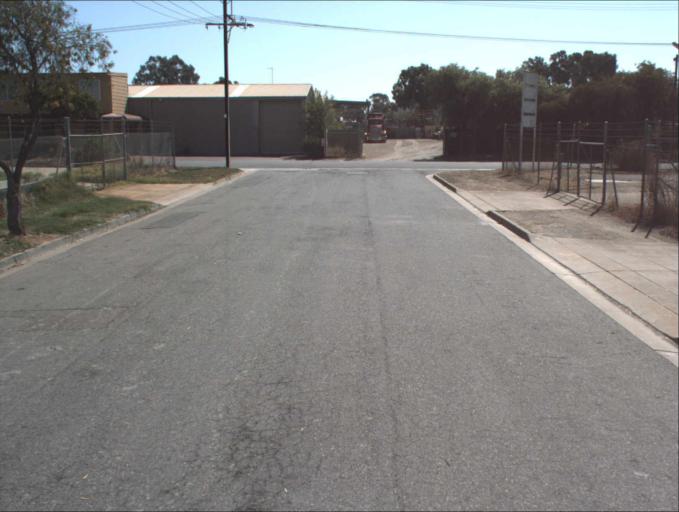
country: AU
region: South Australia
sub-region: Charles Sturt
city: Woodville North
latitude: -34.8375
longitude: 138.5613
